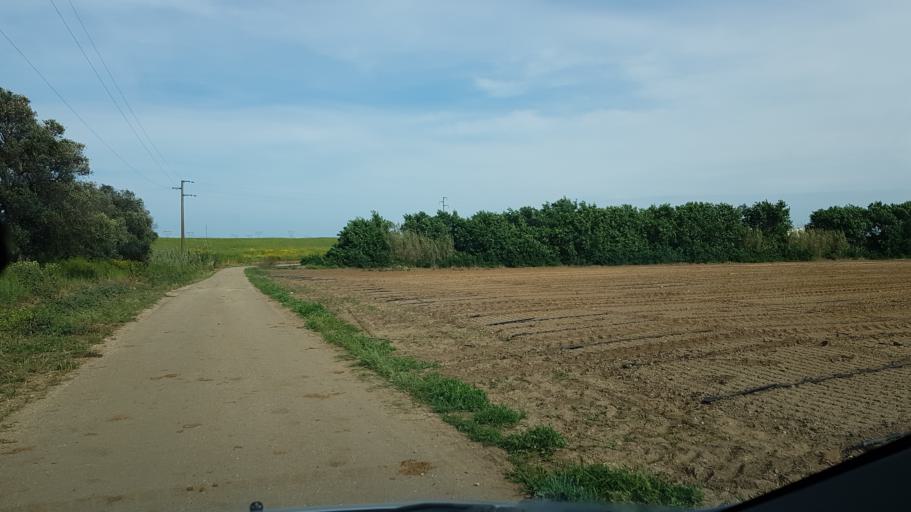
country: IT
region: Apulia
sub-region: Provincia di Brindisi
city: Tuturano
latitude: 40.5611
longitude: 17.9191
